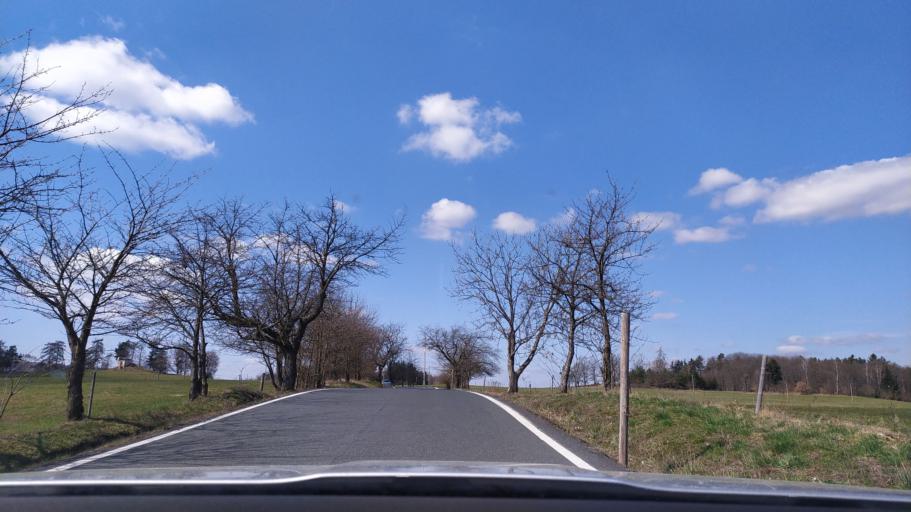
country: DE
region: Bavaria
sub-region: Upper Franconia
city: Hohenberg an der Eger
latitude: 50.1236
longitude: 12.2483
